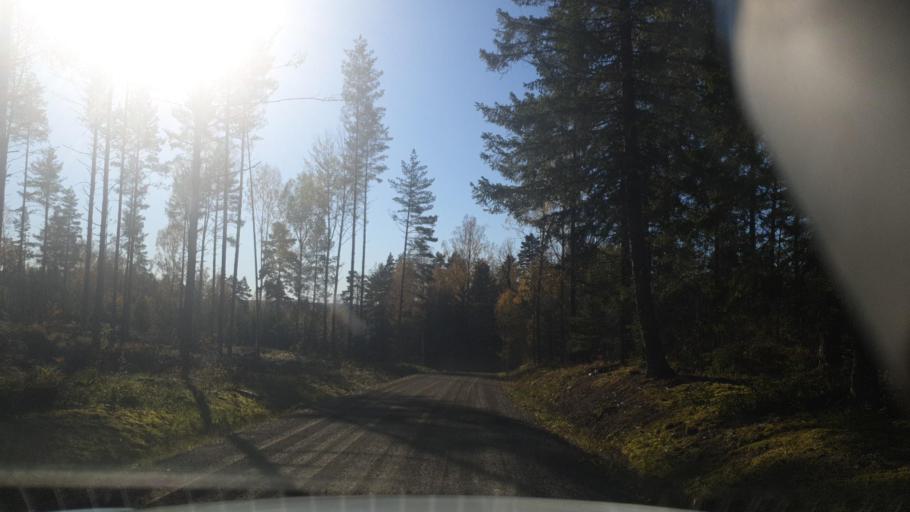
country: SE
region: Vaermland
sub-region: Grums Kommun
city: Slottsbron
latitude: 59.4602
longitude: 12.9183
